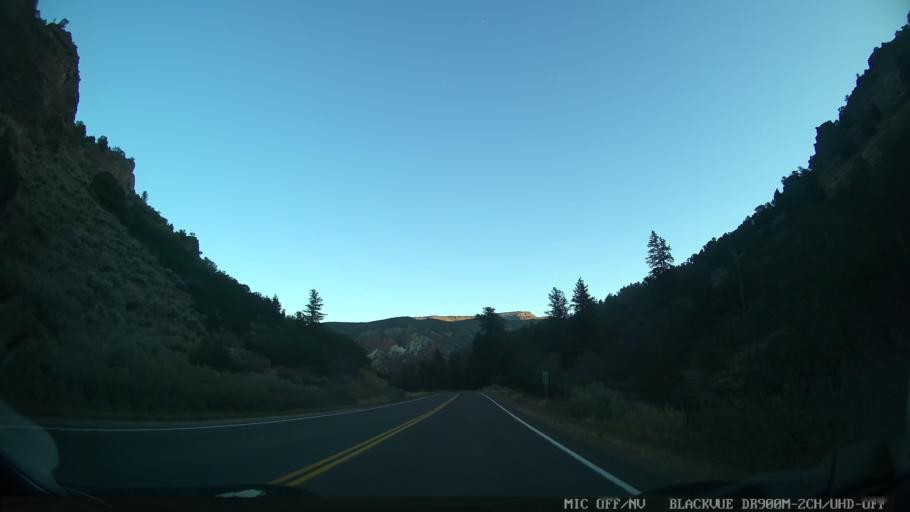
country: US
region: Colorado
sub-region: Eagle County
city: Edwards
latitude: 39.8495
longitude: -106.6437
